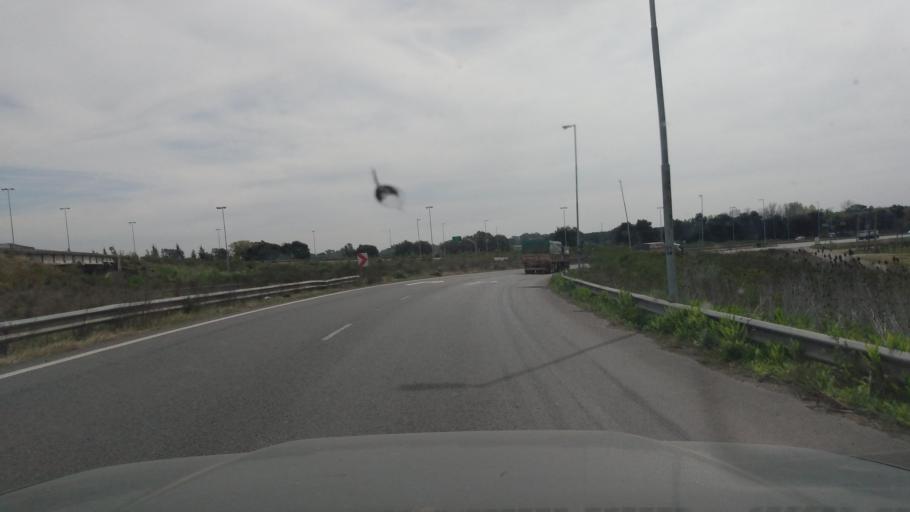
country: AR
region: Buenos Aires
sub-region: Partido de Lujan
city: Lujan
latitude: -34.4716
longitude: -59.0678
